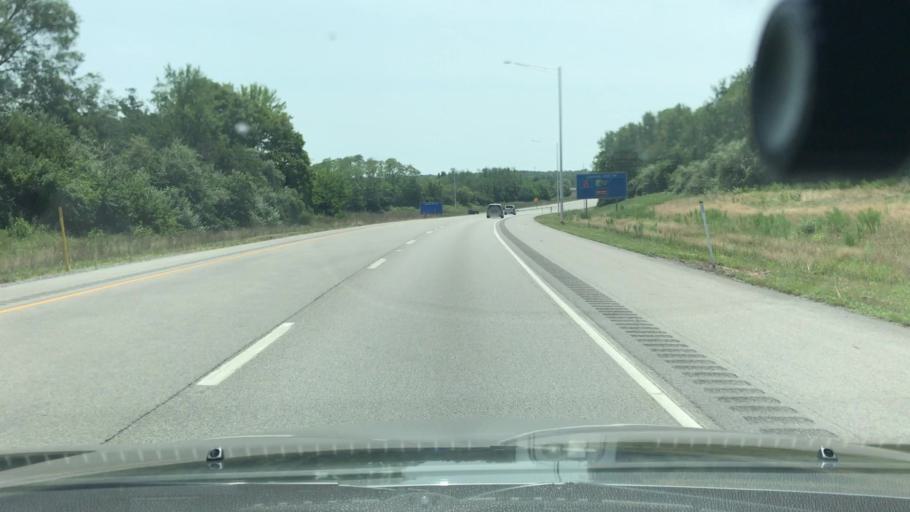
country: US
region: Illinois
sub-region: Jefferson County
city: Mount Vernon
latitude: 38.3356
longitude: -88.9582
